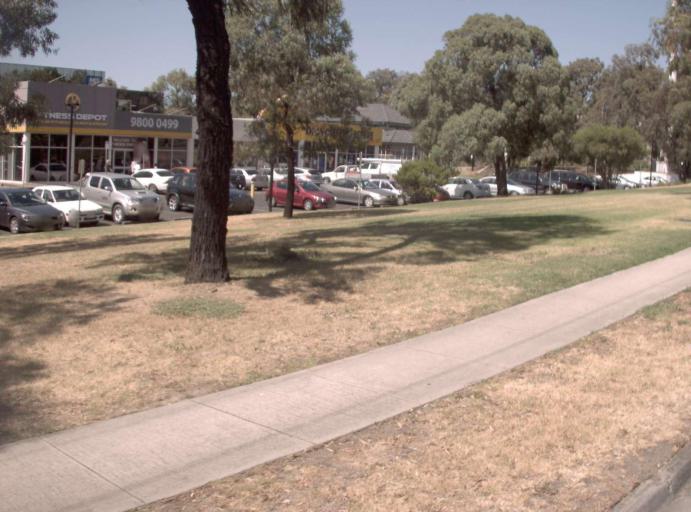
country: AU
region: Victoria
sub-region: Knox
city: Knoxfield
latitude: -37.8713
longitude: 145.2429
